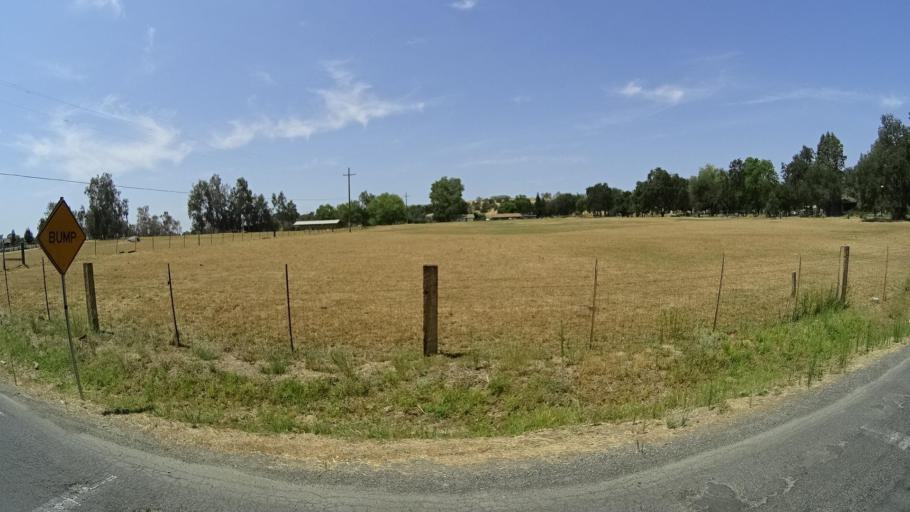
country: US
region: California
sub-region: Placer County
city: Loomis
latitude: 38.8133
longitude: -121.2193
